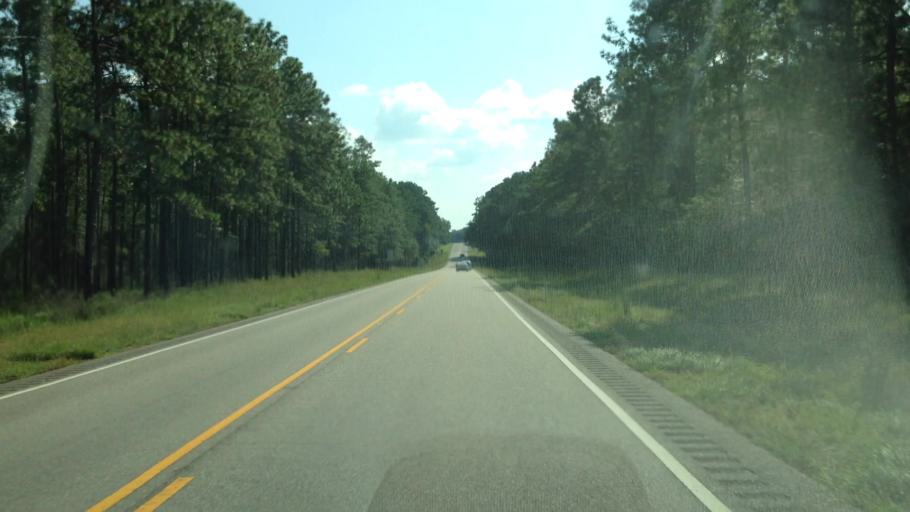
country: US
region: Florida
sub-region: Okaloosa County
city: Crestview
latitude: 30.9990
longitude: -86.6265
